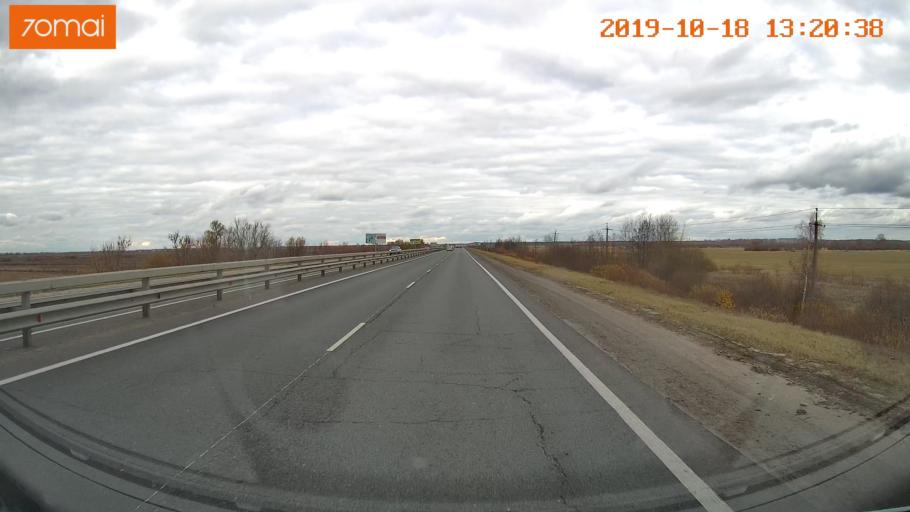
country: RU
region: Rjazan
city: Polyany
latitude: 54.6838
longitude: 39.8335
